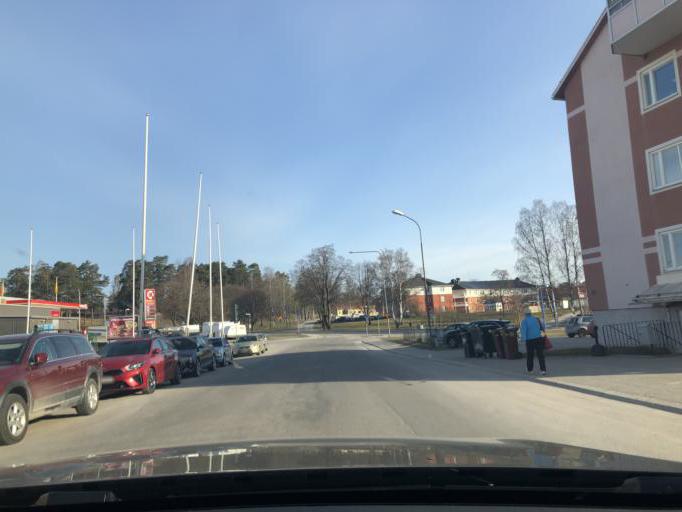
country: SE
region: Gaevleborg
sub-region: Hudiksvalls Kommun
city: Hudiksvall
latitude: 61.7329
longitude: 17.1023
